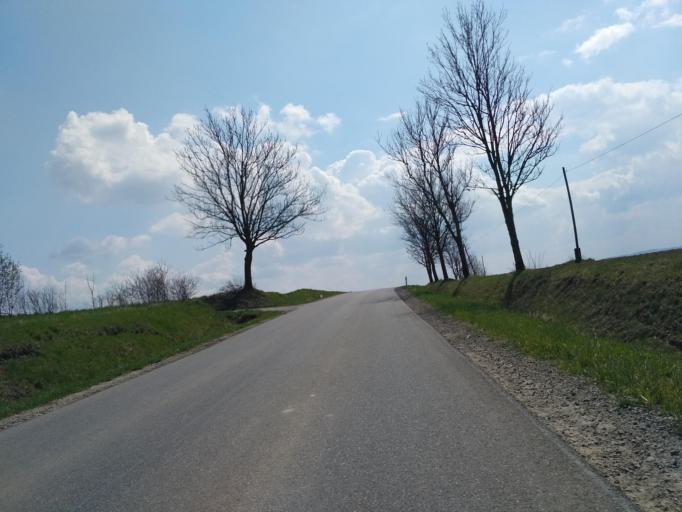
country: PL
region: Subcarpathian Voivodeship
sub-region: Powiat sanocki
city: Bukowsko
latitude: 49.4961
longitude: 22.0420
